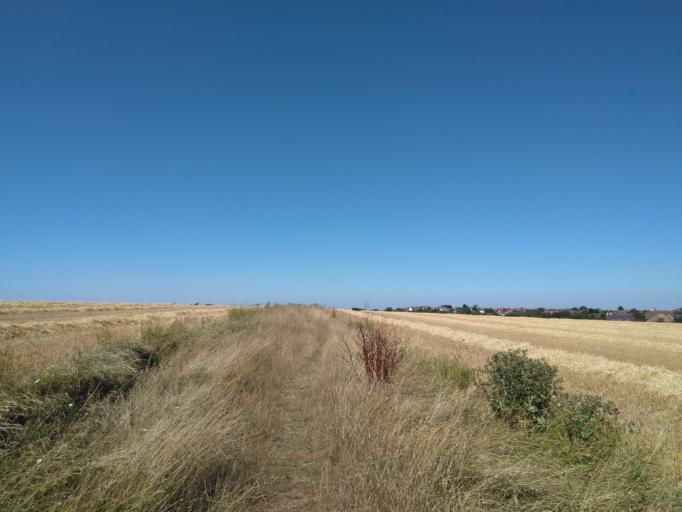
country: GB
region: England
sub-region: Kent
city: Tankerton
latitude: 51.3532
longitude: 1.0493
